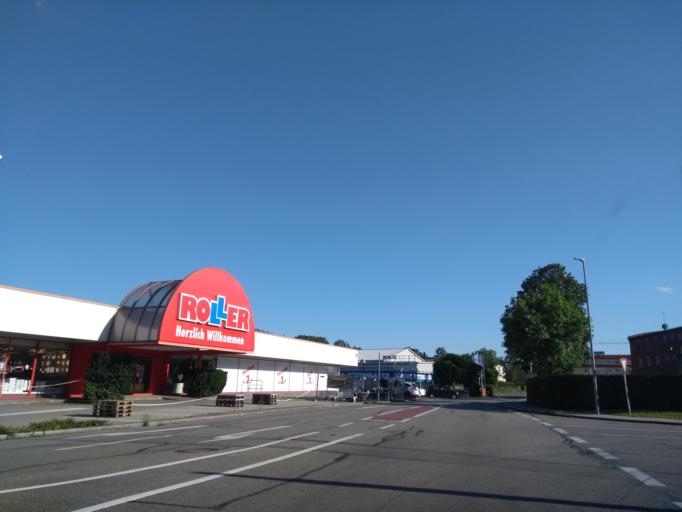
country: DE
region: Bavaria
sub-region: Upper Bavaria
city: Polling
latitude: 48.2360
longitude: 12.5471
